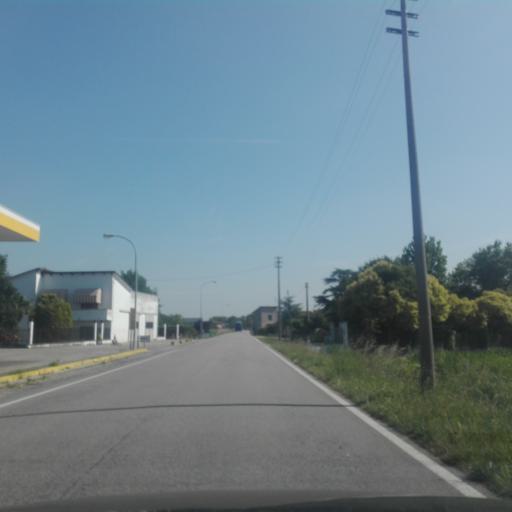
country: IT
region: Veneto
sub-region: Provincia di Rovigo
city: Gavello
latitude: 45.0286
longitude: 11.9169
